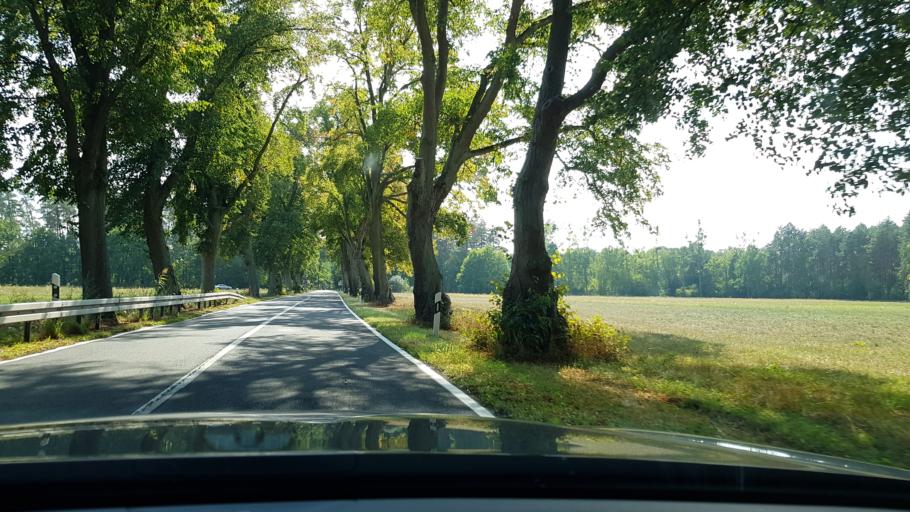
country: DE
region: Brandenburg
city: Lindow
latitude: 53.0102
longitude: 12.9793
